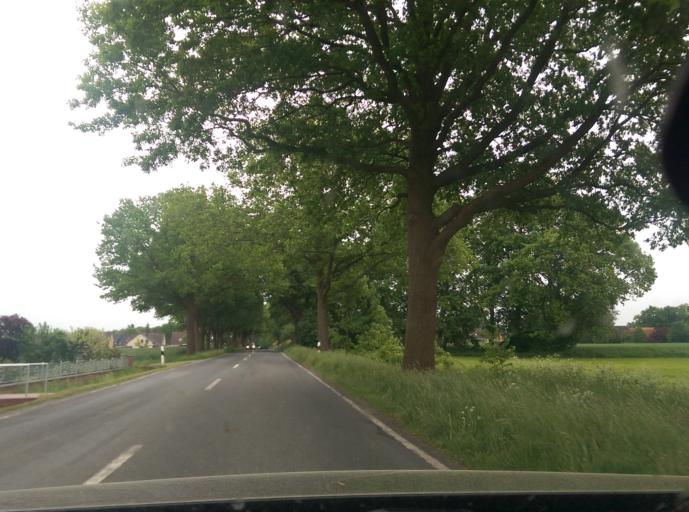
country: DE
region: Lower Saxony
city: Elze
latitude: 52.5244
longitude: 9.6949
